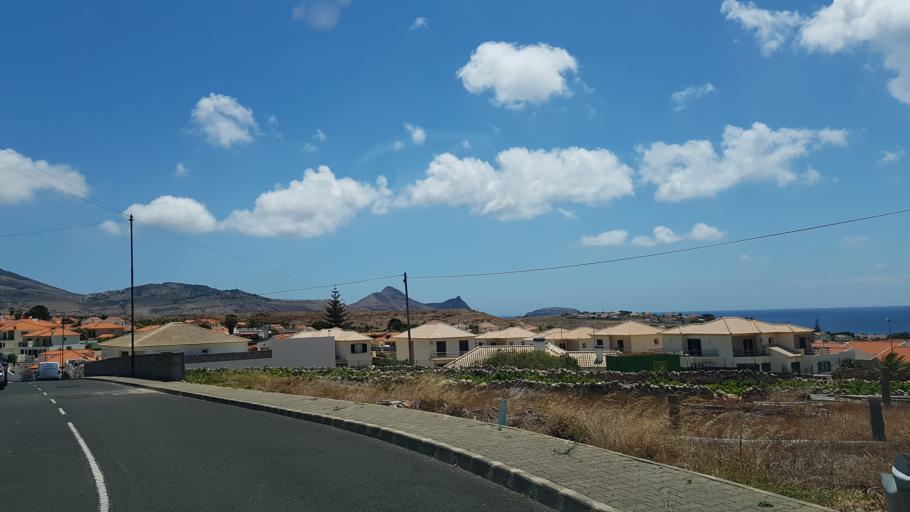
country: PT
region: Madeira
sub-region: Porto Santo
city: Vila de Porto Santo
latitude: 33.0561
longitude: -16.3575
